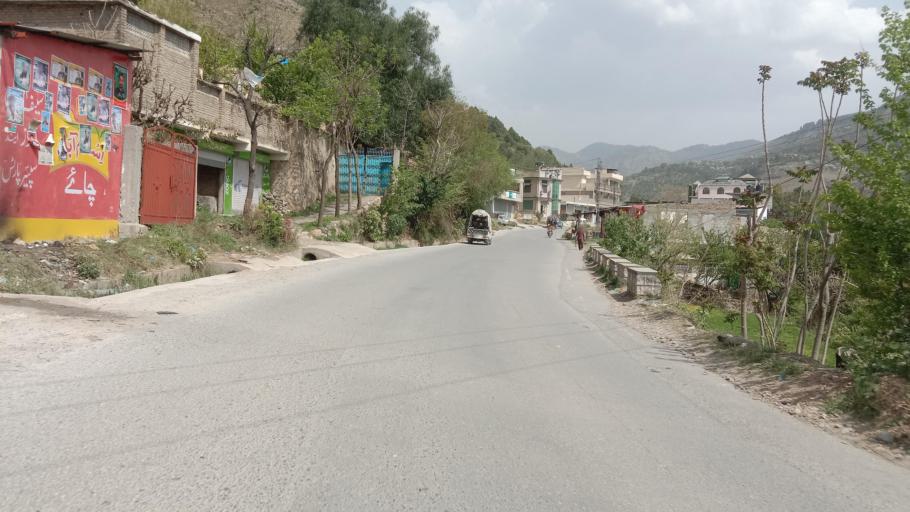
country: PK
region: Khyber Pakhtunkhwa
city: Abbottabad
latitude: 34.1400
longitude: 73.2819
